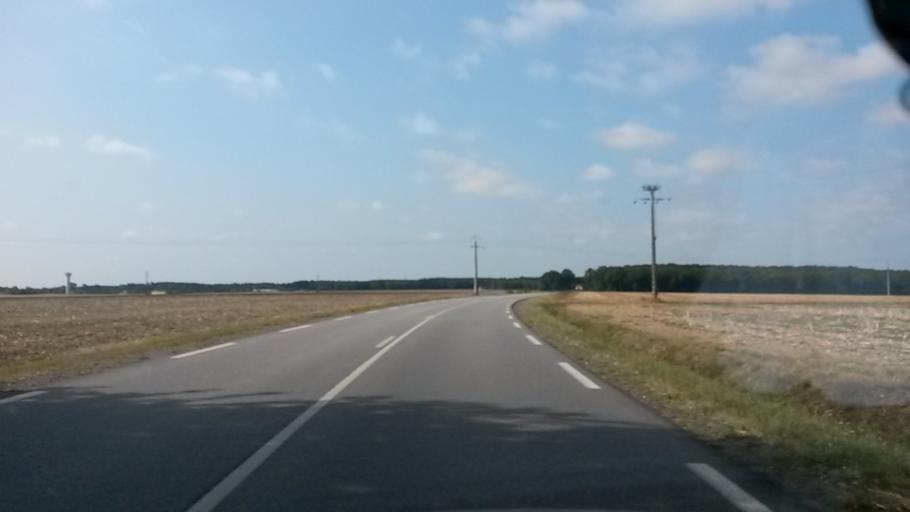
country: FR
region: Haute-Normandie
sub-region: Departement de l'Eure
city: Damville
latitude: 48.8534
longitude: 1.0603
